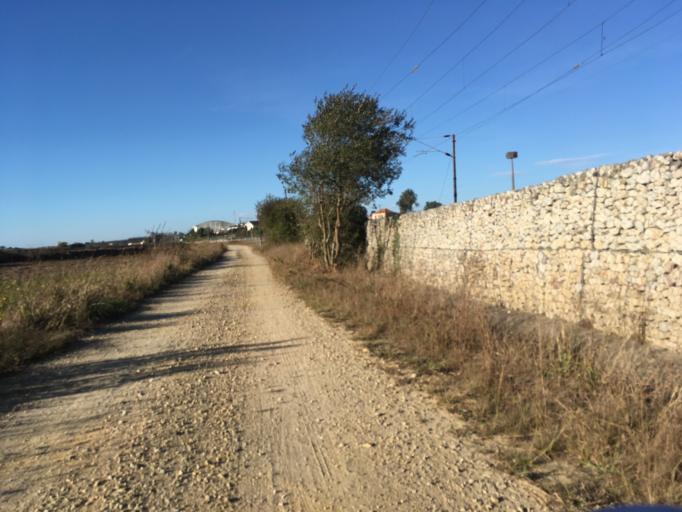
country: PT
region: Aveiro
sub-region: Estarreja
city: Salreu
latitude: 40.7242
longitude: -8.5642
